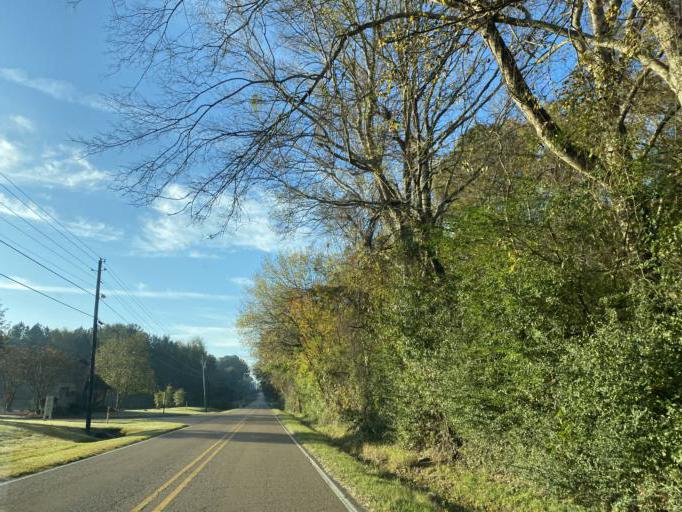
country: US
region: Mississippi
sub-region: Madison County
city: Madison
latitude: 32.4782
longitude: -90.0719
